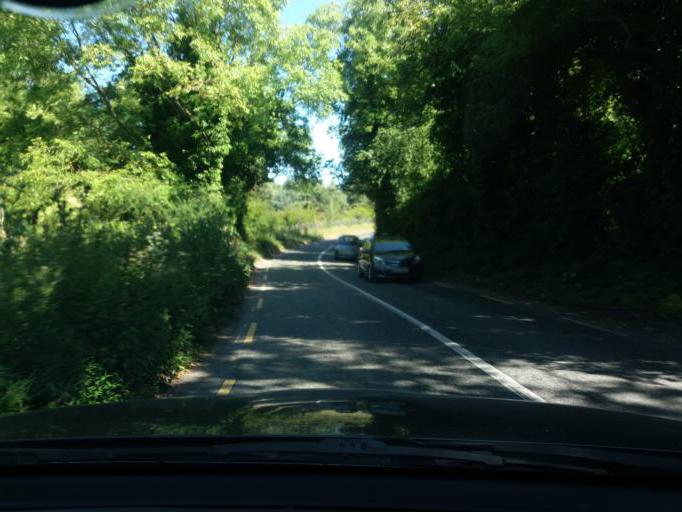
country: IE
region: Leinster
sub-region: Fingal County
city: Swords
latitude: 53.4778
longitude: -6.2737
